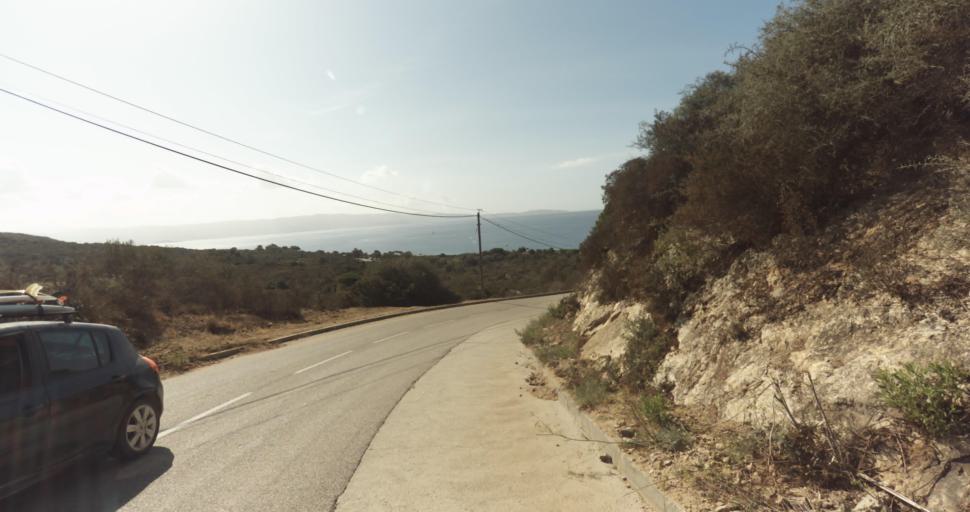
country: FR
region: Corsica
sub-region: Departement de la Corse-du-Sud
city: Ajaccio
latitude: 41.9156
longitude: 8.6440
